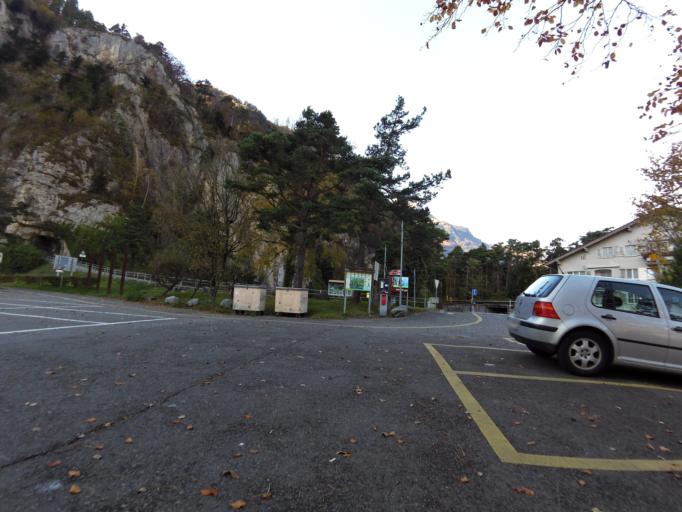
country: CH
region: Uri
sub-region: Uri
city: Bauen
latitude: 46.9174
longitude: 8.5954
